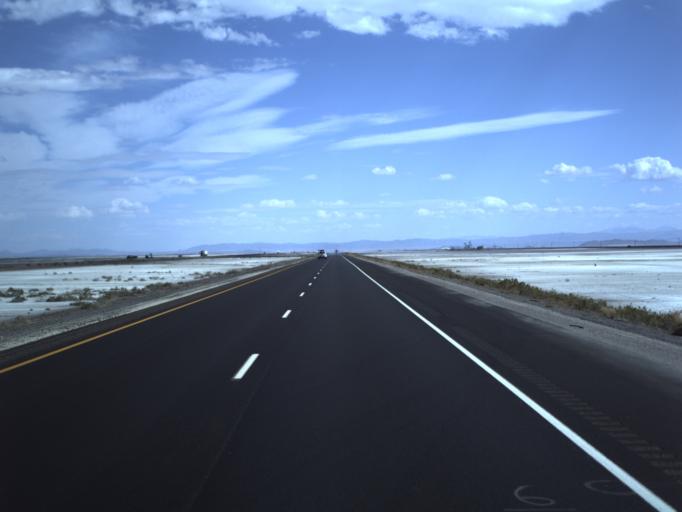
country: US
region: Utah
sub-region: Tooele County
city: Wendover
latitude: 40.7310
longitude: -113.5063
